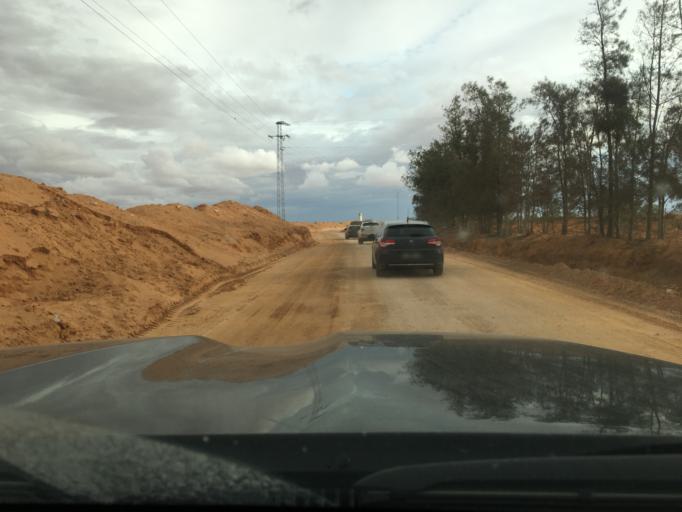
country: TN
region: Madanin
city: Medenine
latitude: 33.2733
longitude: 10.5646
